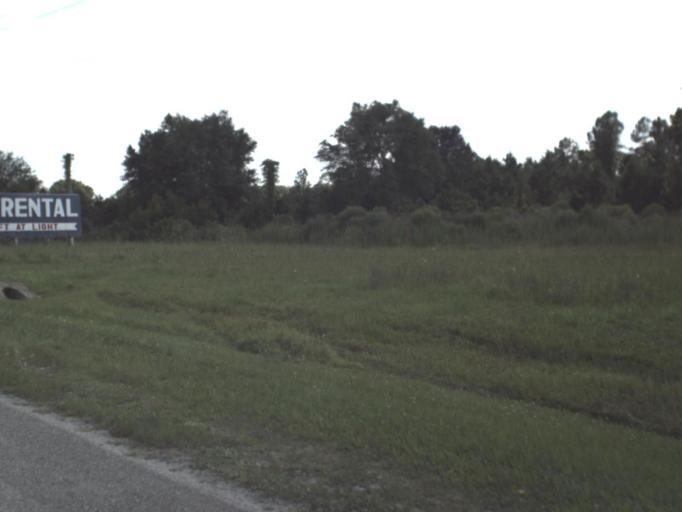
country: US
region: Florida
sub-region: Alachua County
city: Waldo
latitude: 29.8194
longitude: -82.1678
